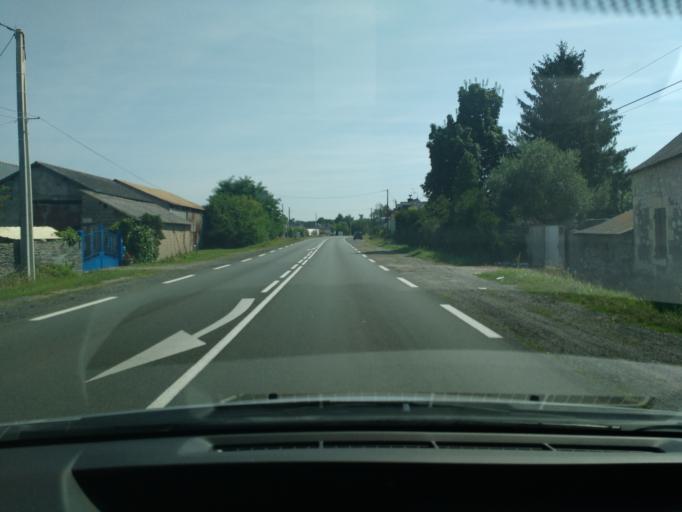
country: FR
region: Pays de la Loire
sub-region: Departement de Maine-et-Loire
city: Corne
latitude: 47.4746
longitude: -0.3279
